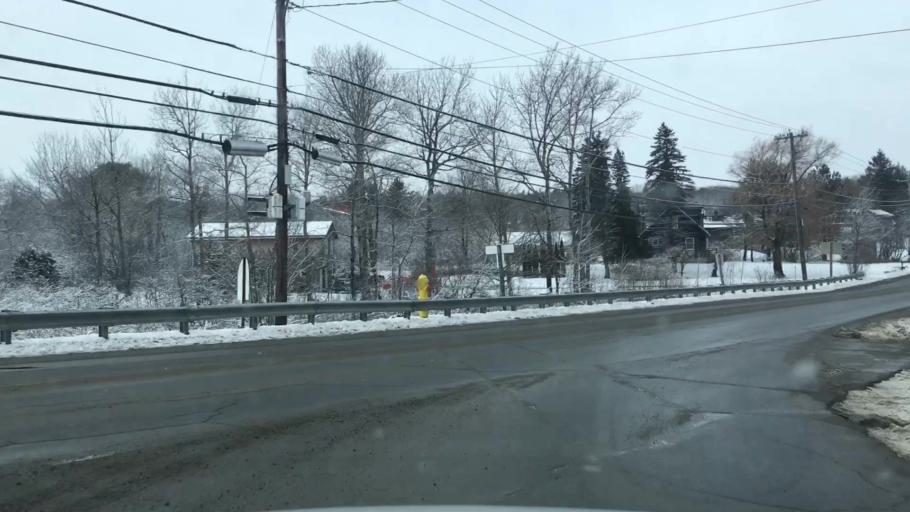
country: US
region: Maine
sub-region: Knox County
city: Rockland
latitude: 44.0767
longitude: -69.1053
